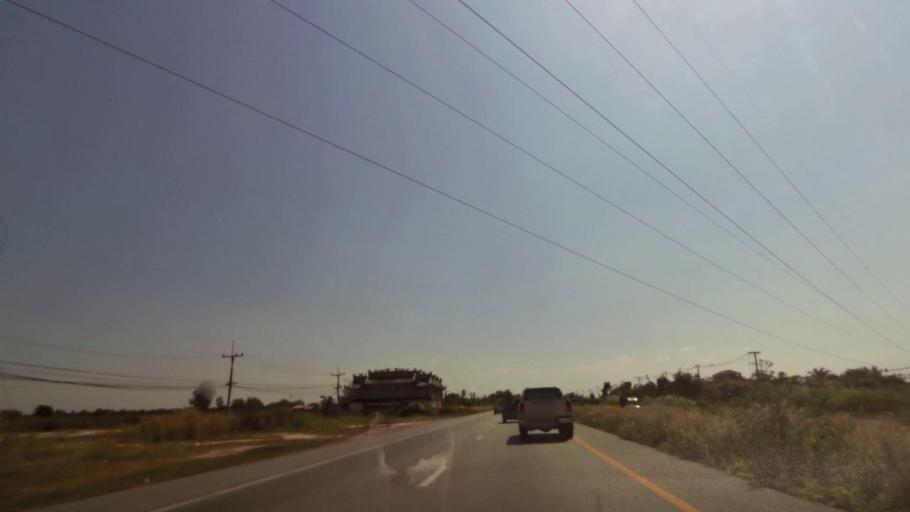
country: TH
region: Nakhon Sawan
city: Kao Liao
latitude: 15.8293
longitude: 100.1186
